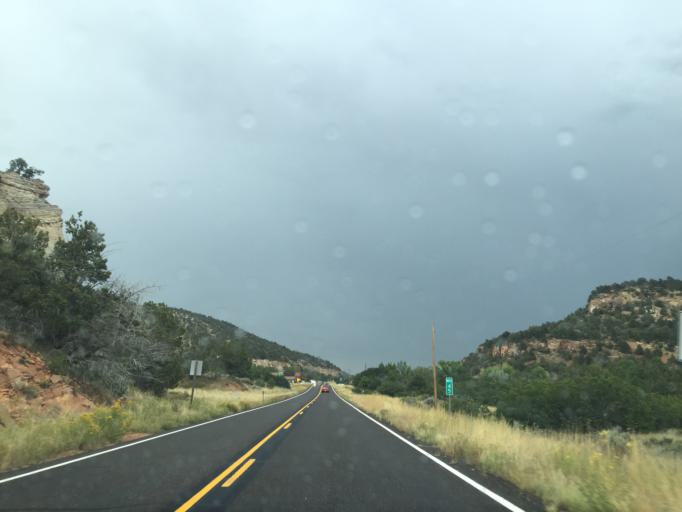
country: US
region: Utah
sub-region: Washington County
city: Hildale
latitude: 37.2362
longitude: -112.8597
